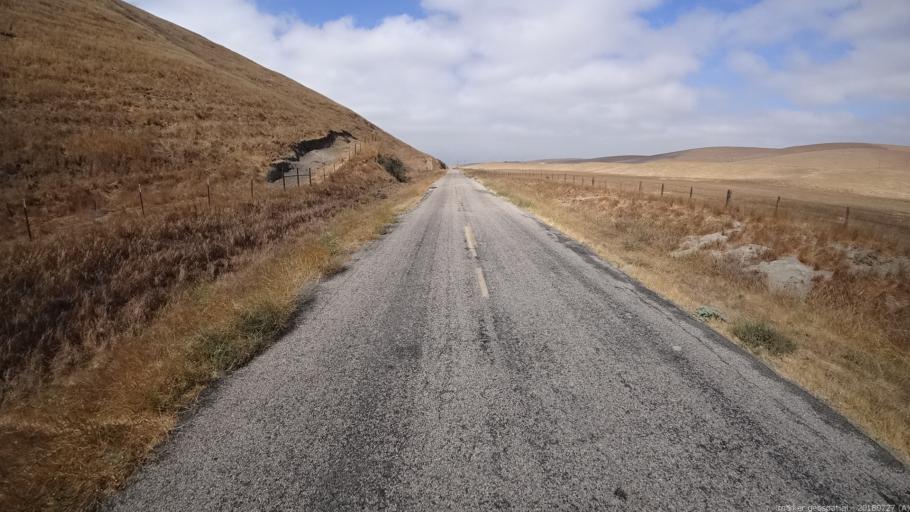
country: US
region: California
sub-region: Monterey County
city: King City
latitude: 36.2312
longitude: -121.0496
